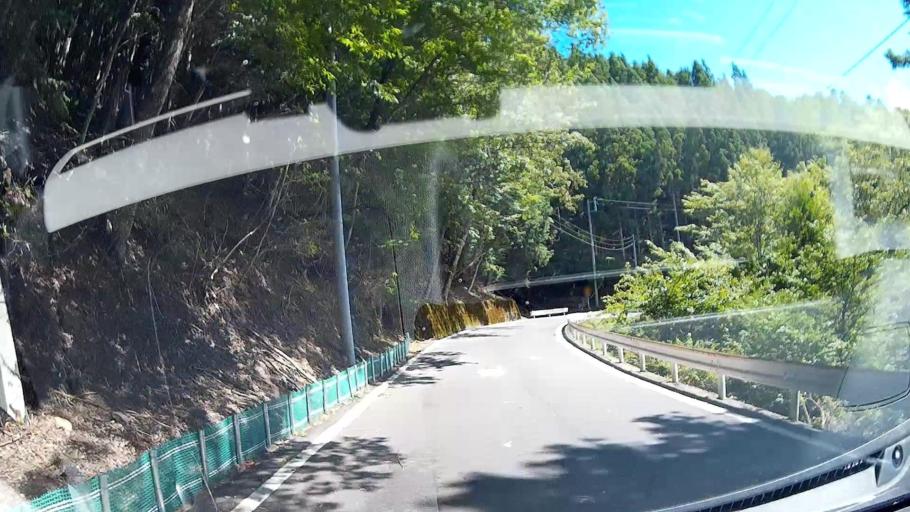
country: JP
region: Shizuoka
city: Shizuoka-shi
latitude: 35.1981
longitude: 138.2460
